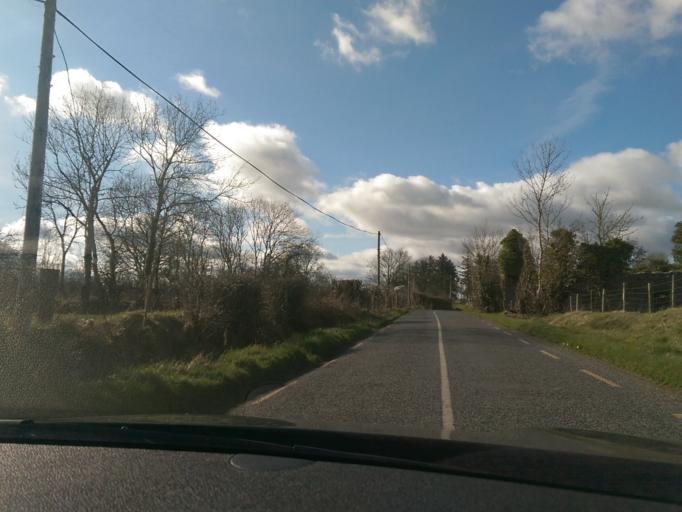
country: IE
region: Connaught
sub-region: County Galway
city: Athenry
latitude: 53.4419
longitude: -8.5614
